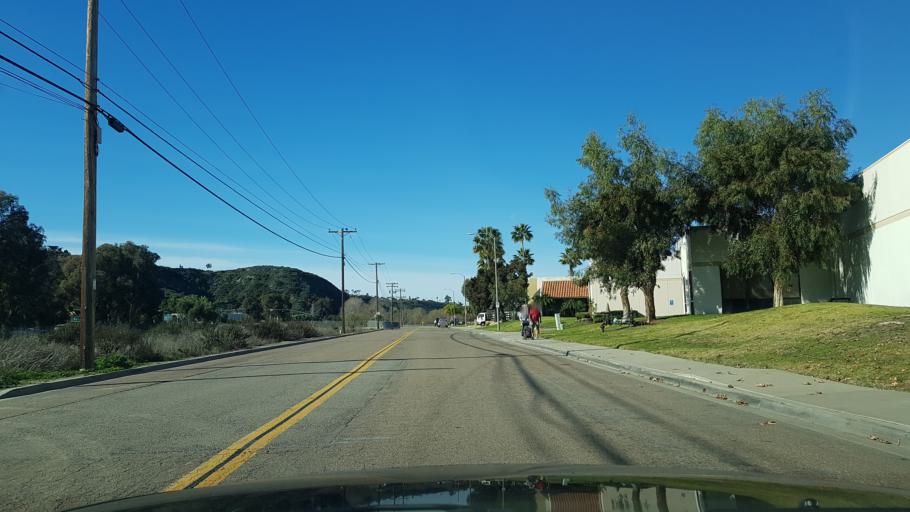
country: US
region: California
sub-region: San Diego County
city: Camp Pendleton South
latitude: 33.2161
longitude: -117.3548
